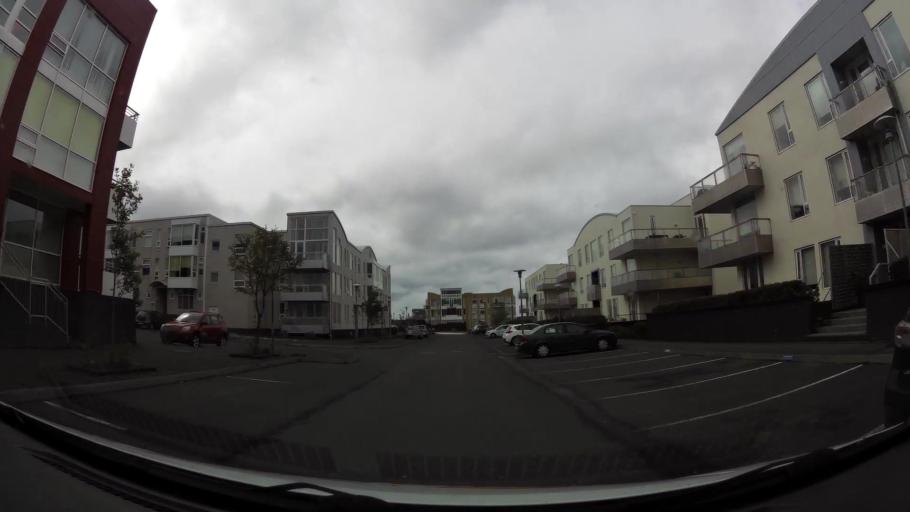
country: IS
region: Capital Region
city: Gardabaer
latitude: 64.0930
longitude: -21.9460
